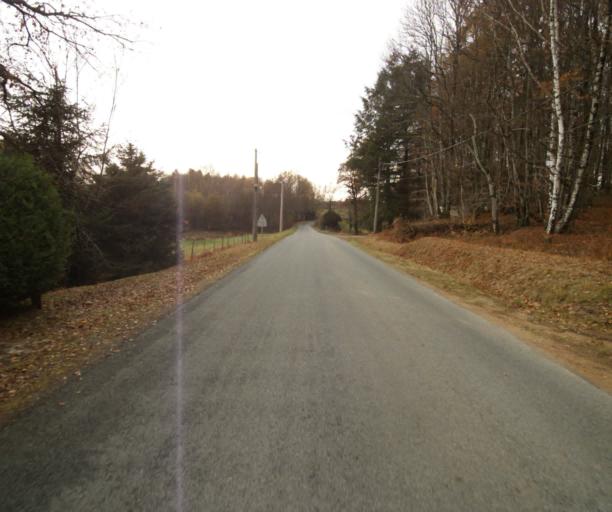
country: FR
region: Limousin
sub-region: Departement de la Correze
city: Sainte-Fortunade
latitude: 45.1771
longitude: 1.7444
